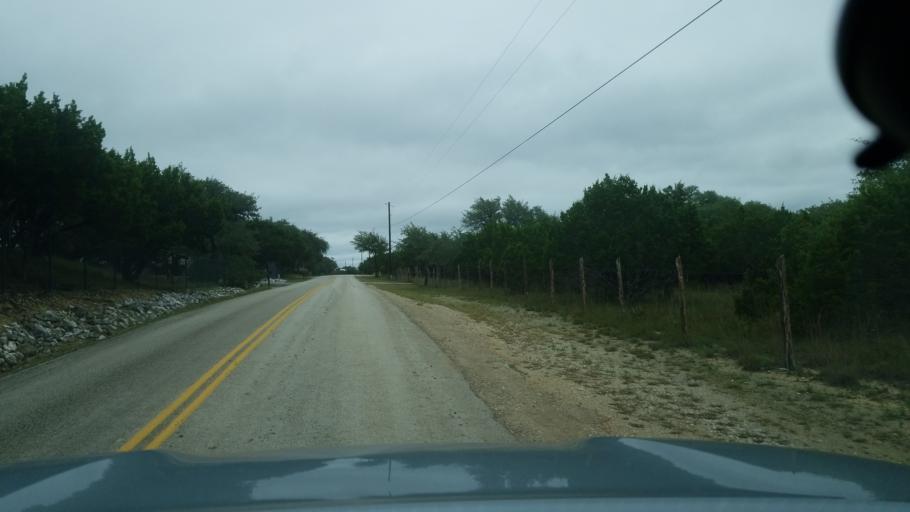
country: US
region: Texas
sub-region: Comal County
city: Bulverde
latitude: 29.7930
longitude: -98.4316
